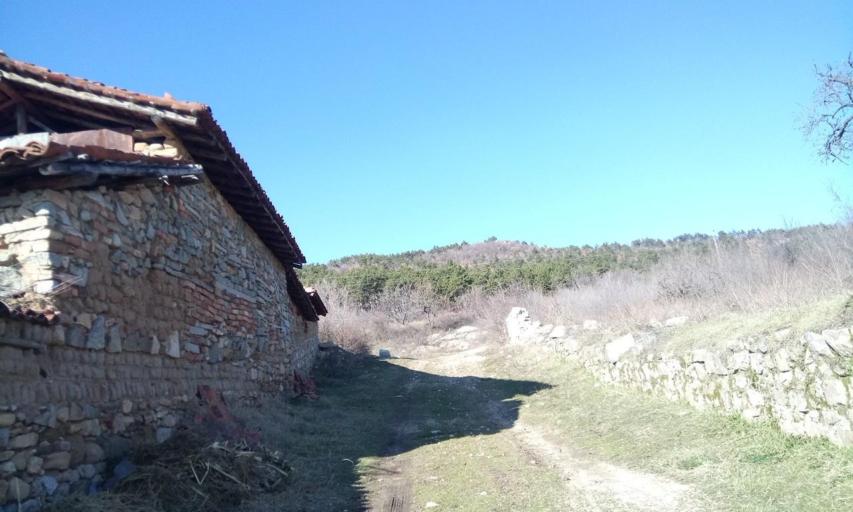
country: BG
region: Plovdiv
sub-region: Obshtina Khisarya
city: Khisarya
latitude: 42.5243
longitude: 24.7192
